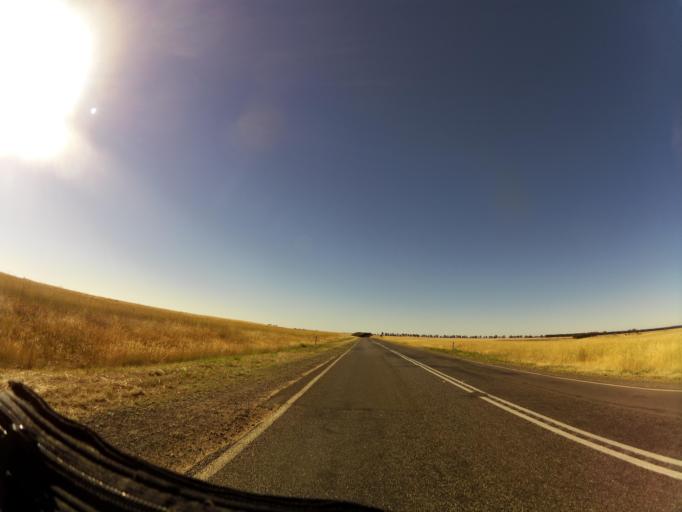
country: AU
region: Victoria
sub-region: Ballarat North
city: Delacombe
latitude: -37.6405
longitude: 143.3459
